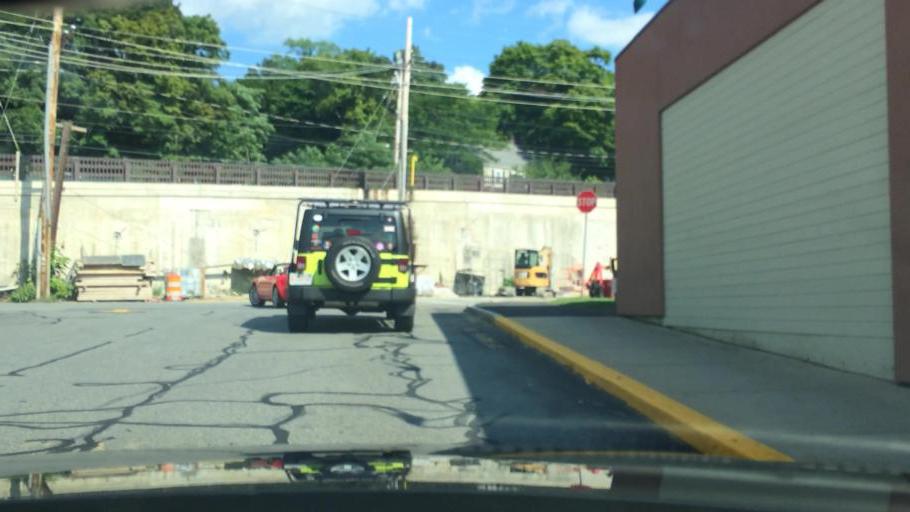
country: US
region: Massachusetts
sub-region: Essex County
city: Andover
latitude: 42.6611
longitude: -71.1445
